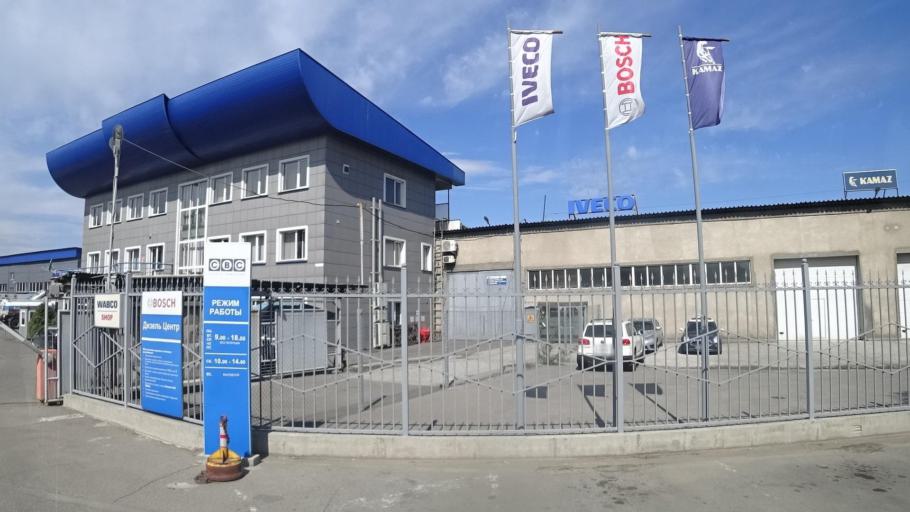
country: KZ
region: Almaty Oblysy
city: Pervomayskiy
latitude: 43.3328
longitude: 76.9748
